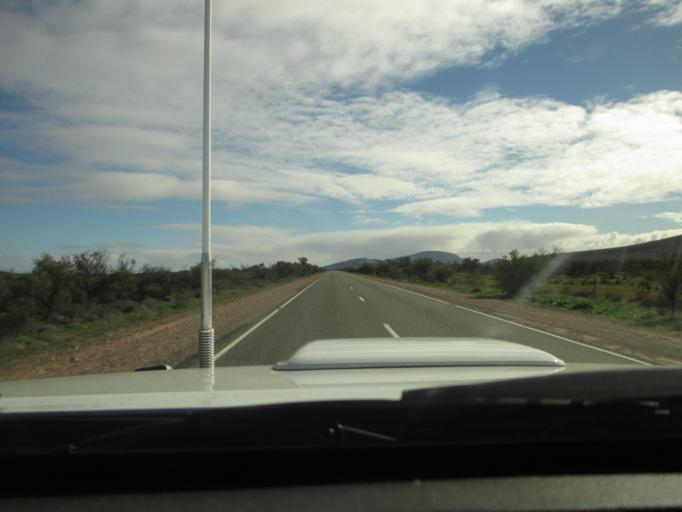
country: AU
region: South Australia
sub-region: Flinders Ranges
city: Quorn
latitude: -31.8514
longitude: 138.3972
